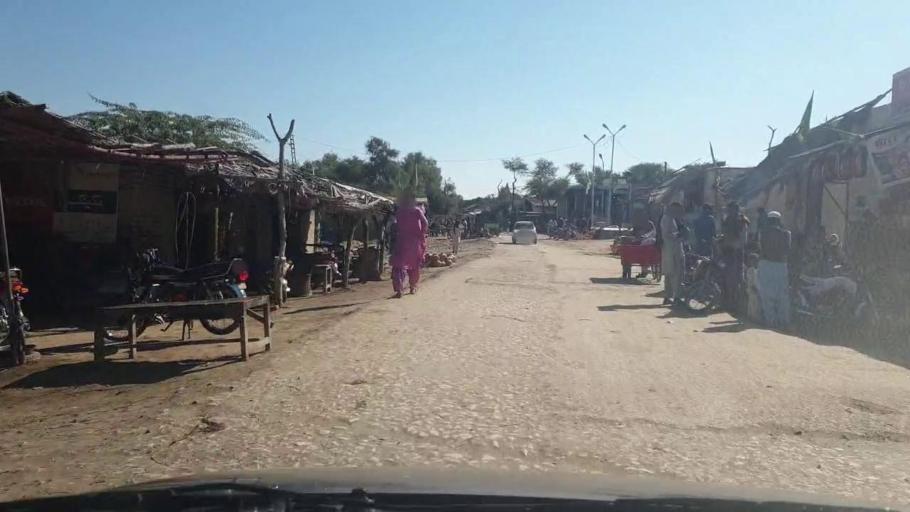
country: PK
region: Sindh
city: Bozdar
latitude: 27.0664
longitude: 68.6173
